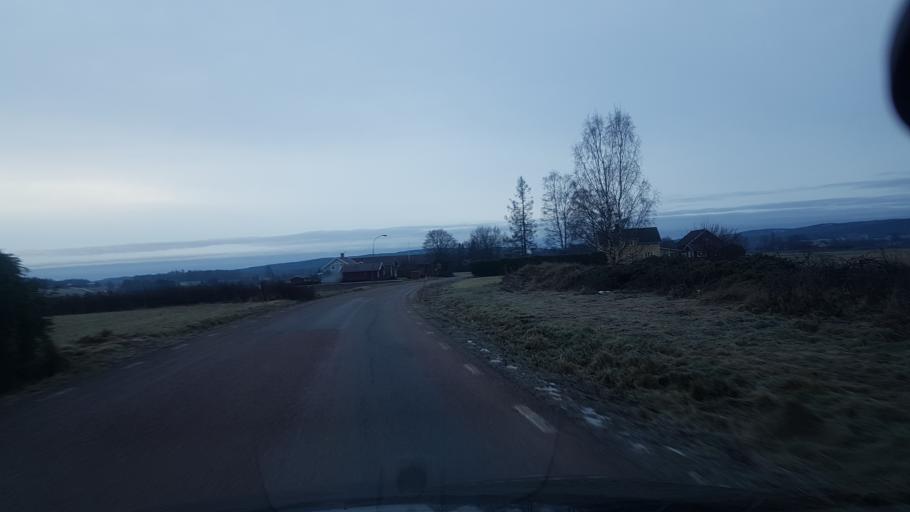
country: SE
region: Dalarna
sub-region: Saters Kommun
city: Saeter
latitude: 60.4297
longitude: 15.6565
